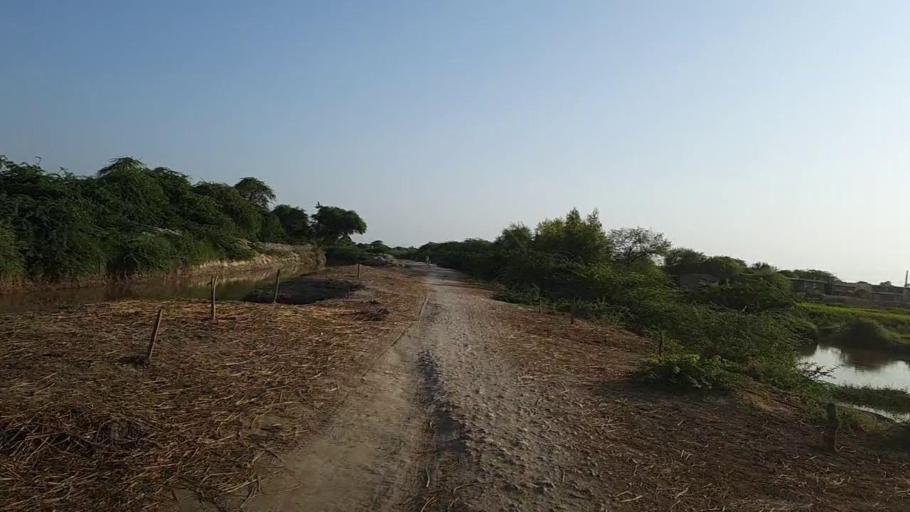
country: PK
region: Sindh
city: Kario
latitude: 24.7332
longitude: 68.6691
